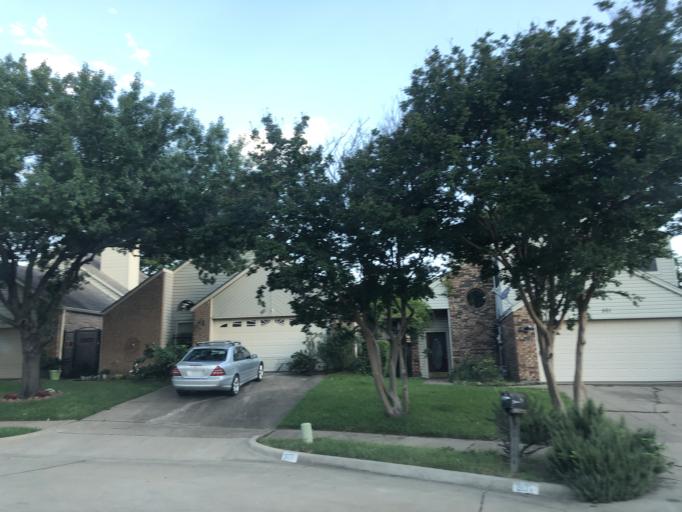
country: US
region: Texas
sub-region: Dallas County
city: Sunnyvale
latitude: 32.8408
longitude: -96.6081
